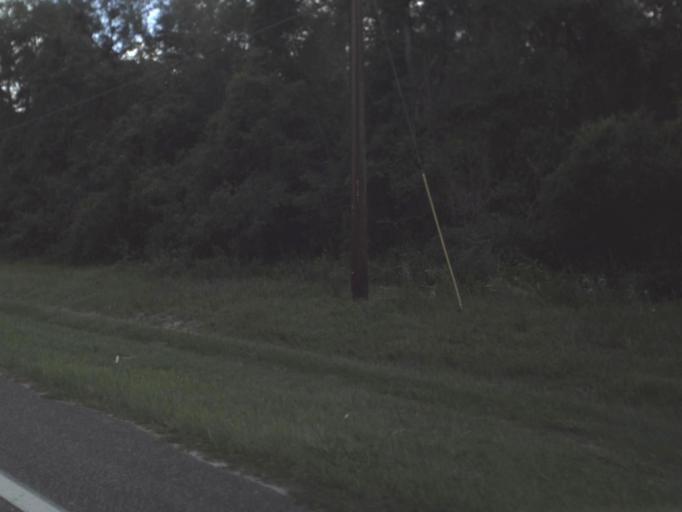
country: US
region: Florida
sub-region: Putnam County
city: Crescent City
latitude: 29.4599
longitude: -81.5211
